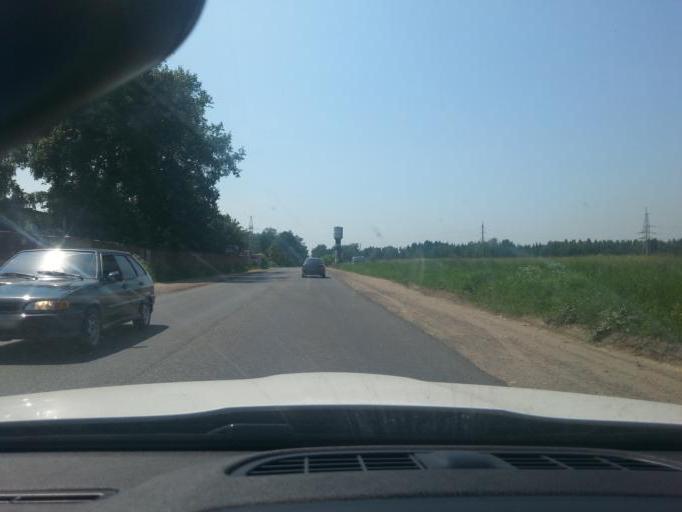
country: RU
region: Moskovskaya
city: Zheleznodorozhnyy
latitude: 55.7234
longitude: 37.9753
